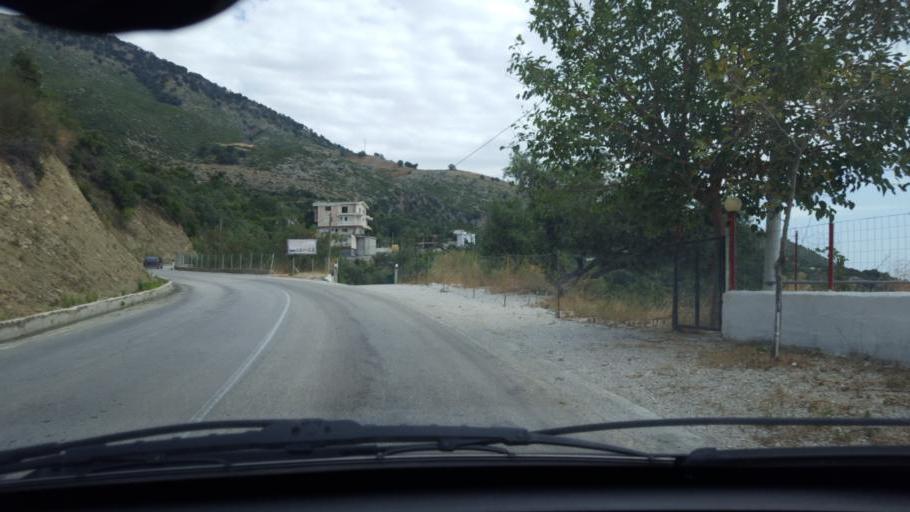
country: AL
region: Vlore
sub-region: Rrethi i Sarandes
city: Lukove
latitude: 40.0558
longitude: 19.8647
